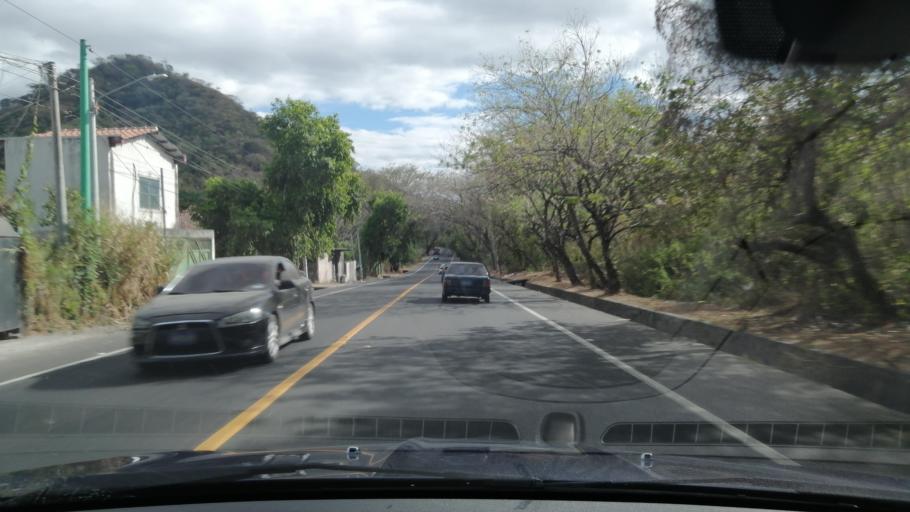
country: SV
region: Santa Ana
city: Santa Ana
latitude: 14.0001
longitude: -89.5416
